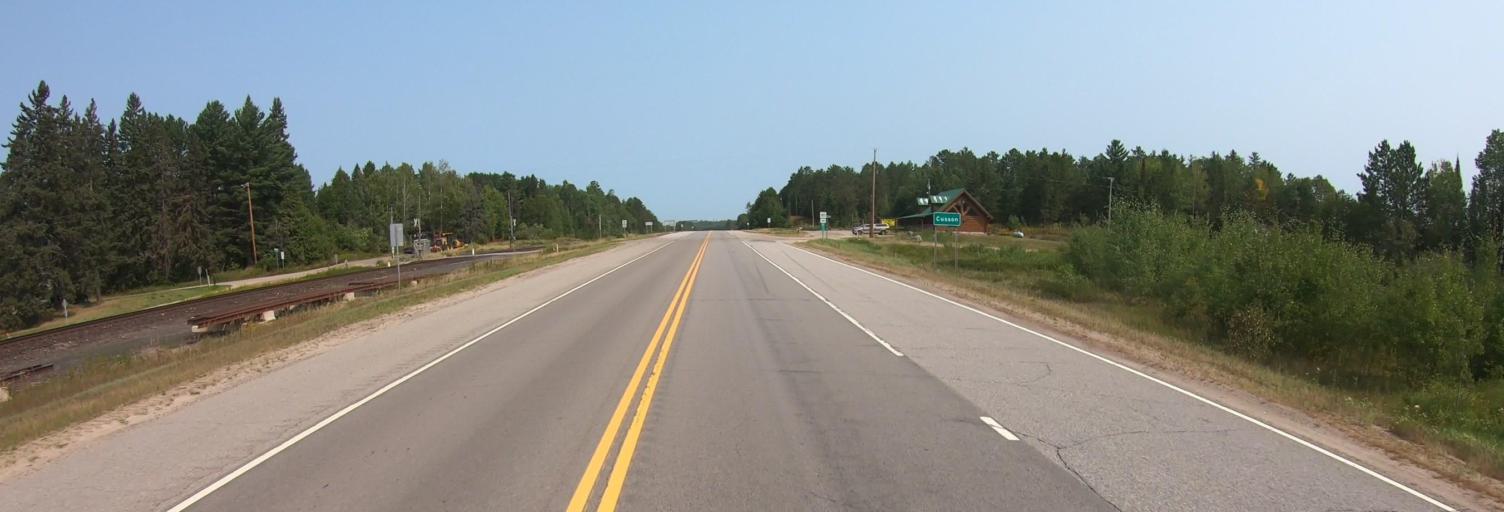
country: US
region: Minnesota
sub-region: Saint Louis County
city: Mountain Iron
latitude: 48.1013
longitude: -92.8436
